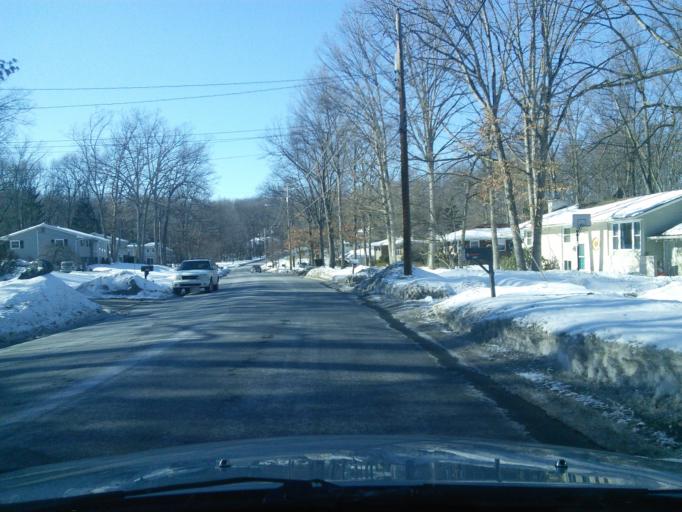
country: US
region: Pennsylvania
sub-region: Centre County
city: Park Forest Village
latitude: 40.8033
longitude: -77.9023
